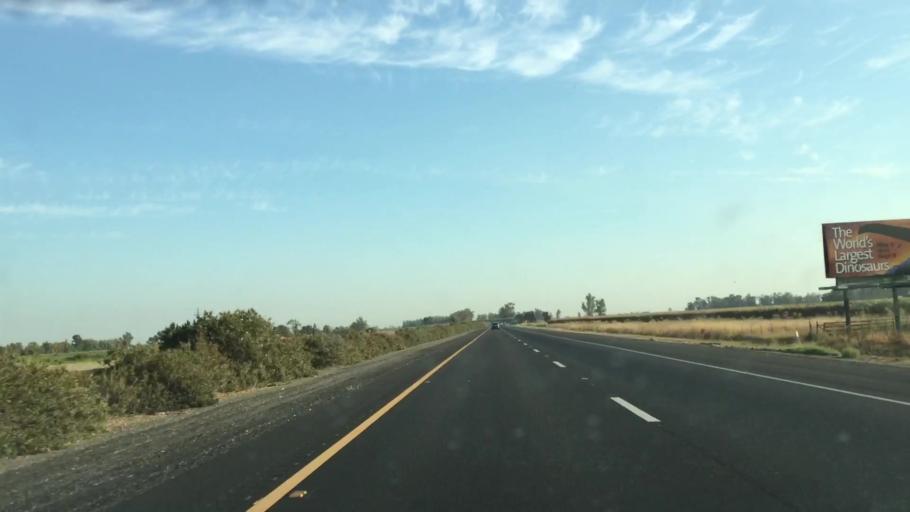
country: US
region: California
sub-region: Glenn County
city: Willows
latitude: 39.5725
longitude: -122.2112
